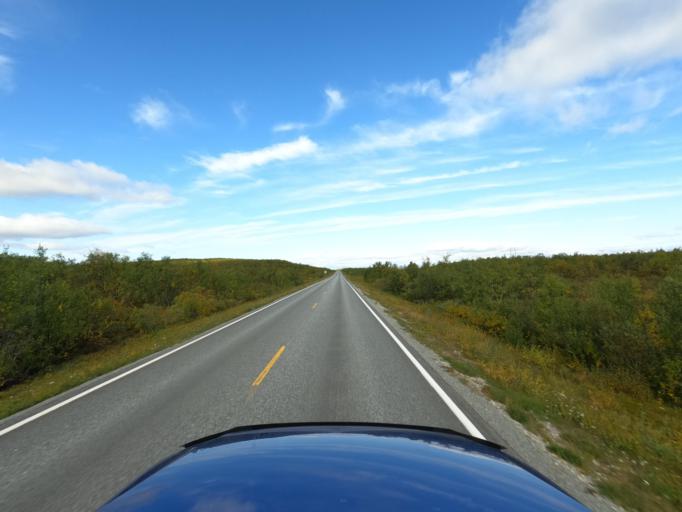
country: NO
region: Finnmark Fylke
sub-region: Karasjok
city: Karasjohka
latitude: 69.6809
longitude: 25.2627
